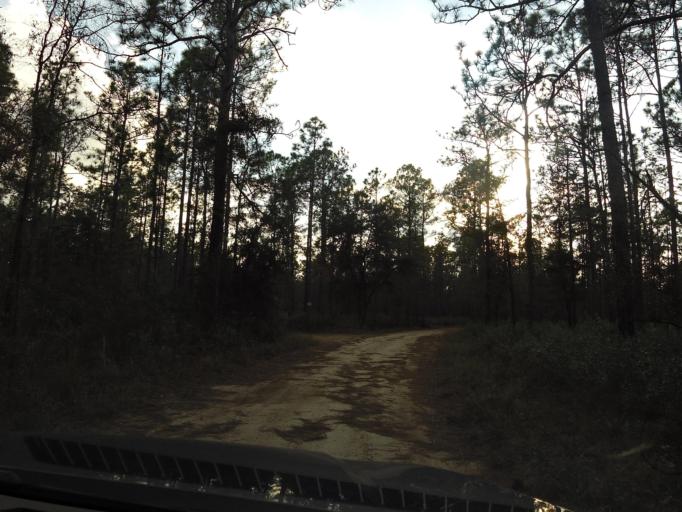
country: US
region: Florida
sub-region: Clay County
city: Middleburg
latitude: 30.1310
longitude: -81.9421
